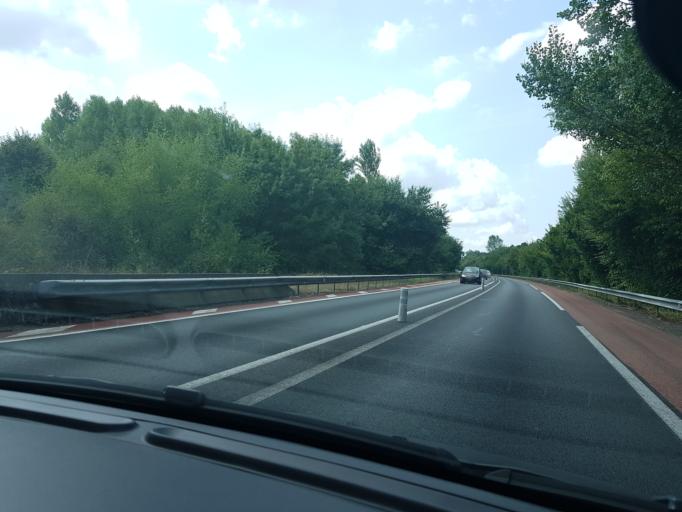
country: FR
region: Aquitaine
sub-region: Departement de la Gironde
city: Arveyres
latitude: 44.8698
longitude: -0.2641
